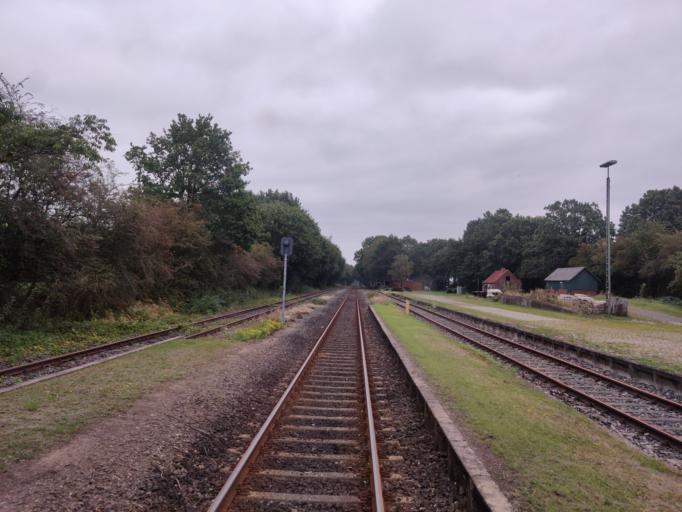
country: DE
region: Lower Saxony
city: Deinste
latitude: 53.5323
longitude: 9.4431
